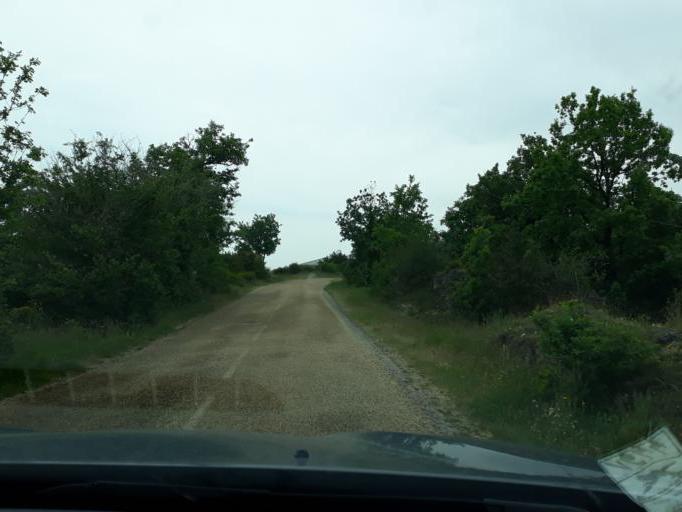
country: FR
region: Languedoc-Roussillon
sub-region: Departement de l'Herault
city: Lodeve
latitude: 43.8473
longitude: 3.2680
